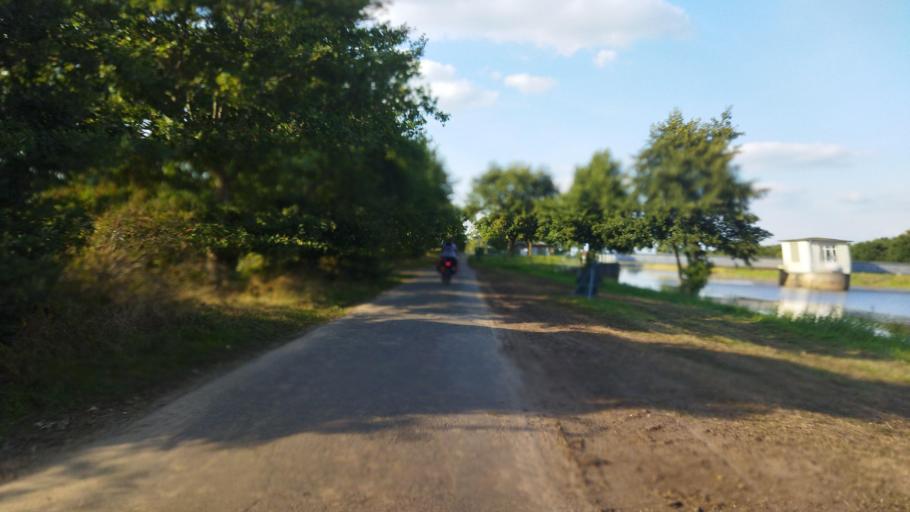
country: DE
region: Lower Saxony
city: Heede
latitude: 53.0305
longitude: 7.3137
